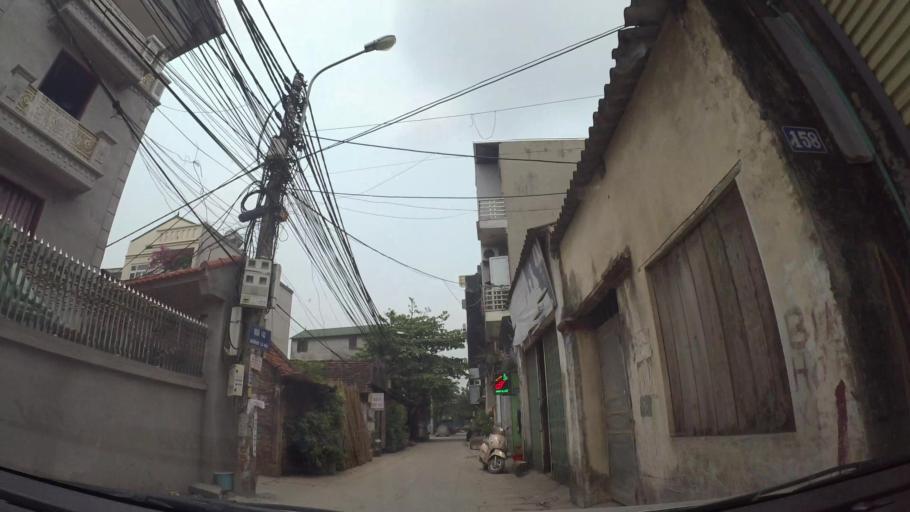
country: VN
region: Ha Noi
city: Ha Dong
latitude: 20.9834
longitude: 105.7489
